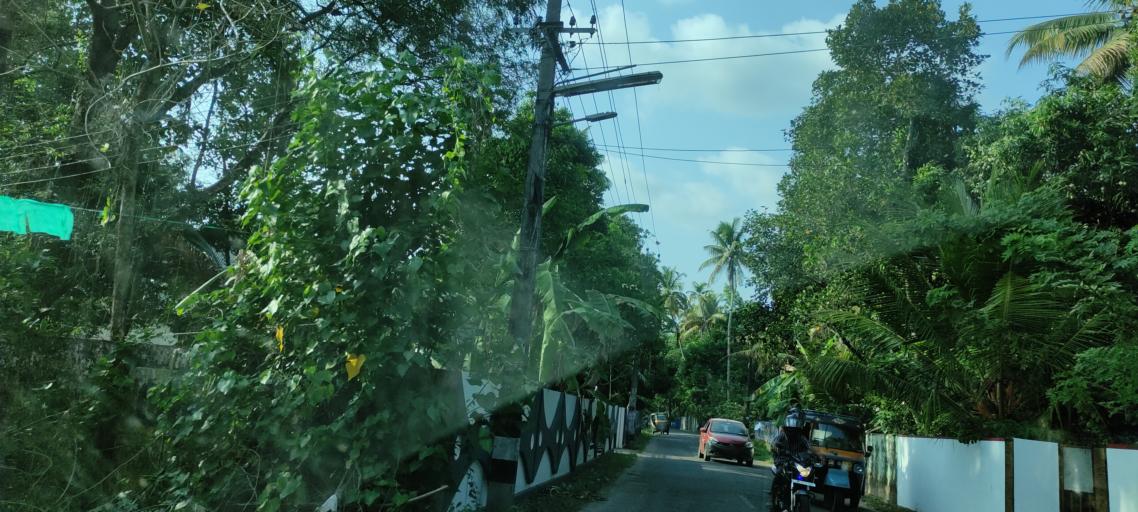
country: IN
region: Kerala
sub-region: Alappuzha
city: Vayalar
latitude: 9.6977
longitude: 76.2900
